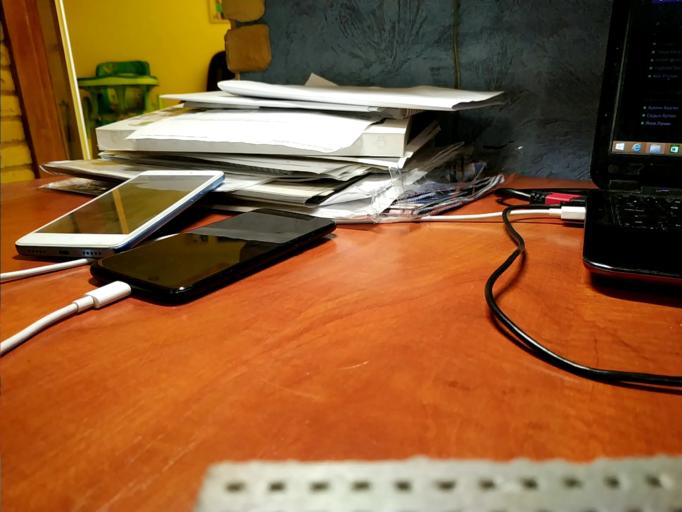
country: RU
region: Tverskaya
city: Kalashnikovo
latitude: 57.4150
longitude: 35.1413
